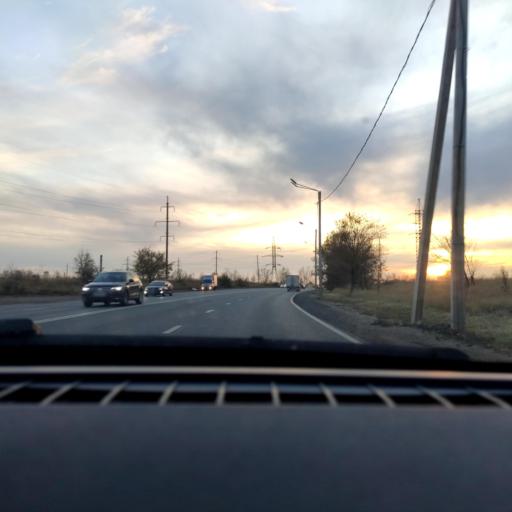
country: RU
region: Voronezj
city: Maslovka
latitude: 51.6225
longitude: 39.2772
